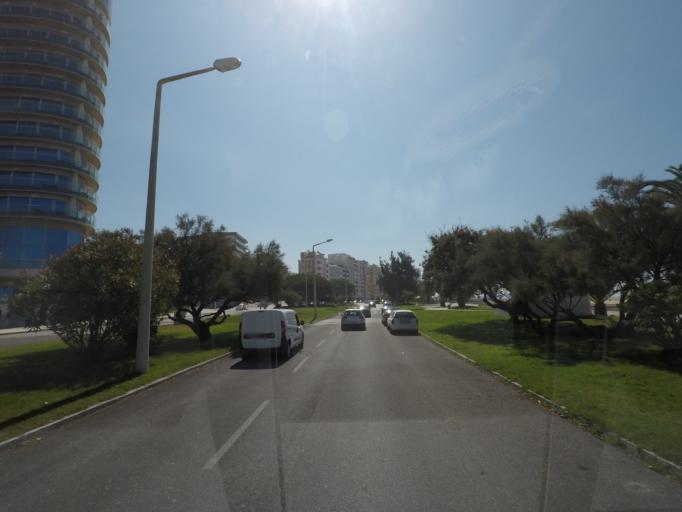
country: PT
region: Coimbra
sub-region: Figueira da Foz
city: Figueira da Foz
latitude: 40.1562
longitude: -8.8680
